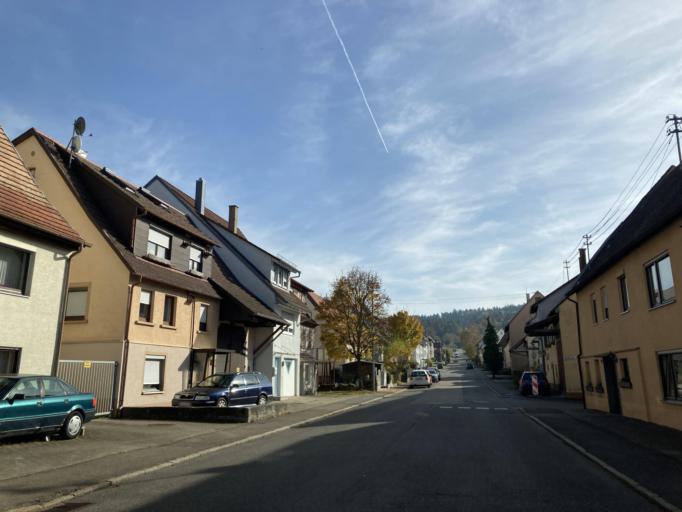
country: DE
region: Baden-Wuerttemberg
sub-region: Tuebingen Region
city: Rottenburg
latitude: 48.4345
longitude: 8.9364
